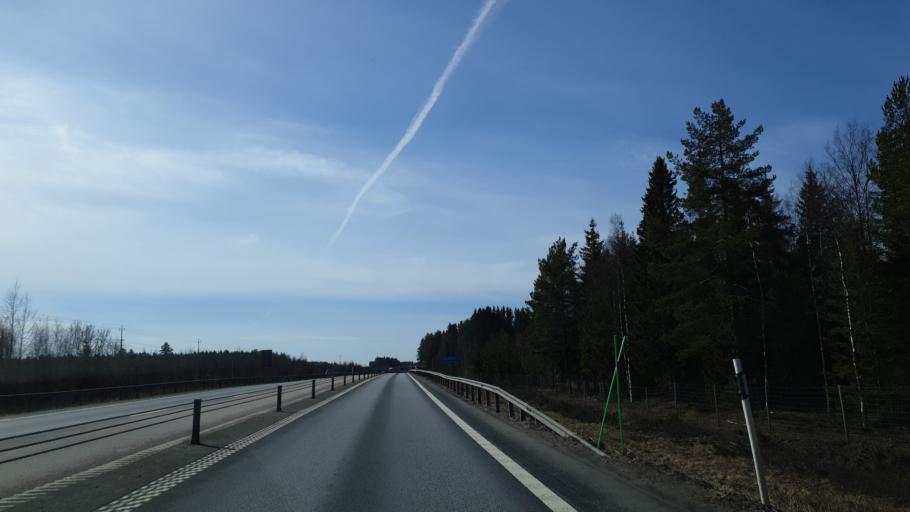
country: SE
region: Vaesterbotten
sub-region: Nordmalings Kommun
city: Nordmaling
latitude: 63.5606
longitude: 19.4264
